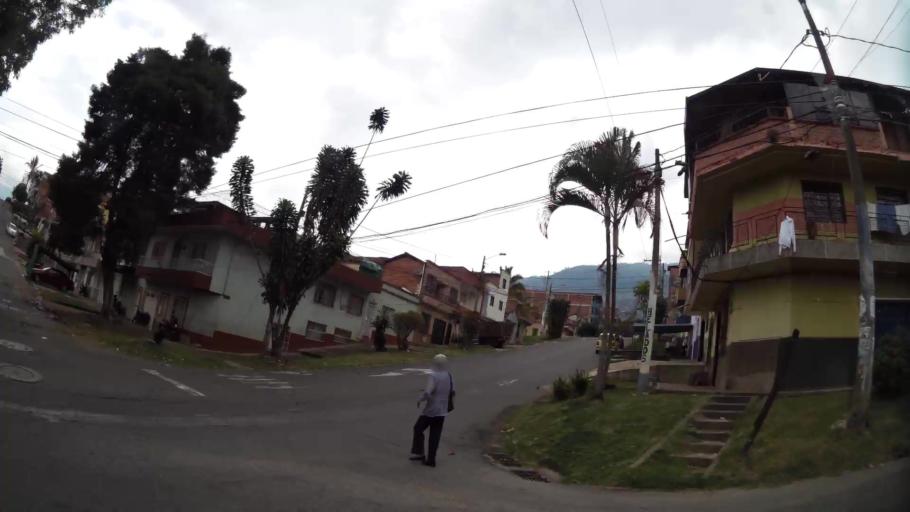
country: CO
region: Antioquia
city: Medellin
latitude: 6.2847
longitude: -75.5609
